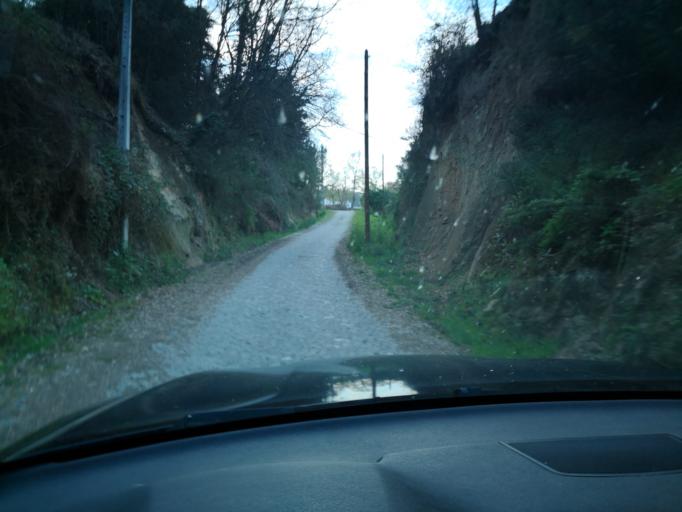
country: PT
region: Vila Real
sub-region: Vila Real
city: Vila Real
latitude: 41.3033
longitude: -7.7738
